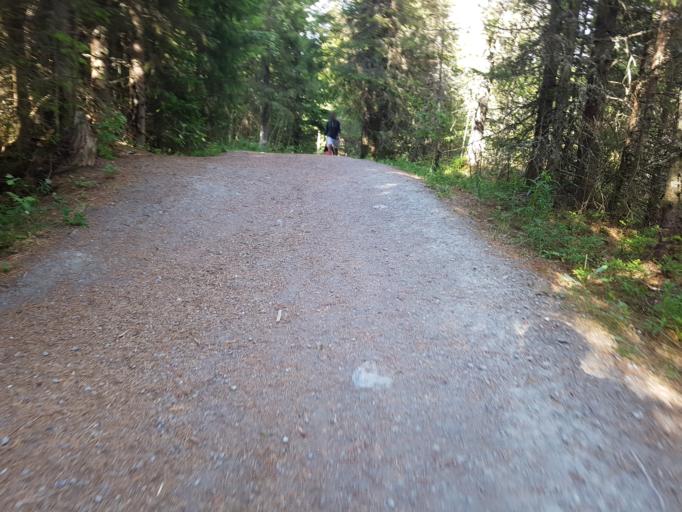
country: NO
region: Sor-Trondelag
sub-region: Trondheim
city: Trondheim
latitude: 63.3989
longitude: 10.3207
